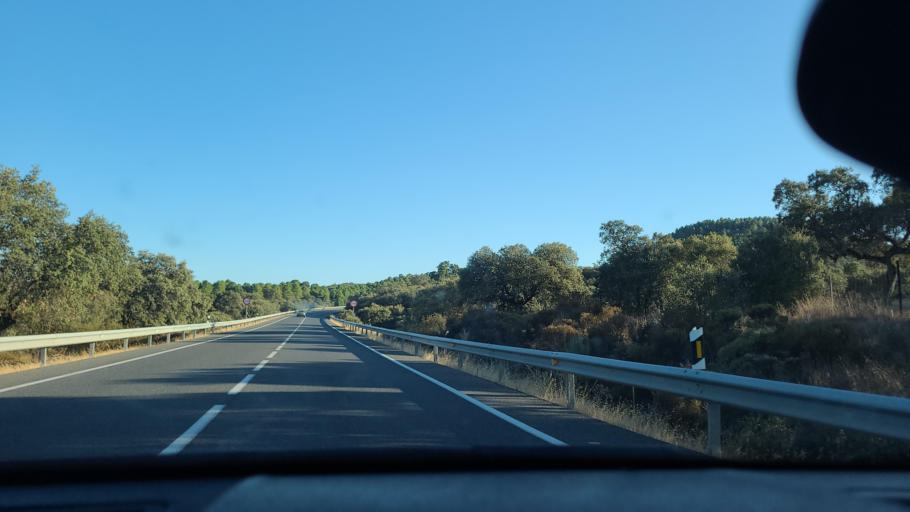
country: ES
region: Andalusia
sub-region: Province of Cordoba
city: Obejo
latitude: 38.0388
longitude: -4.8075
